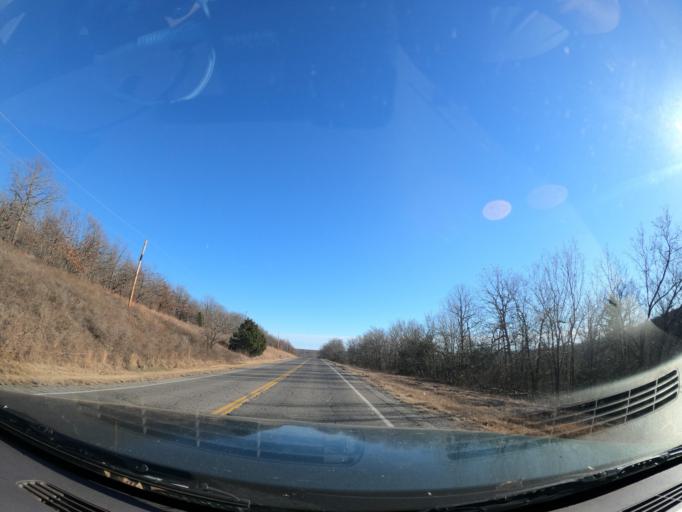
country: US
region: Oklahoma
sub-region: Pittsburg County
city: Longtown
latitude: 35.2187
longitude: -95.4266
